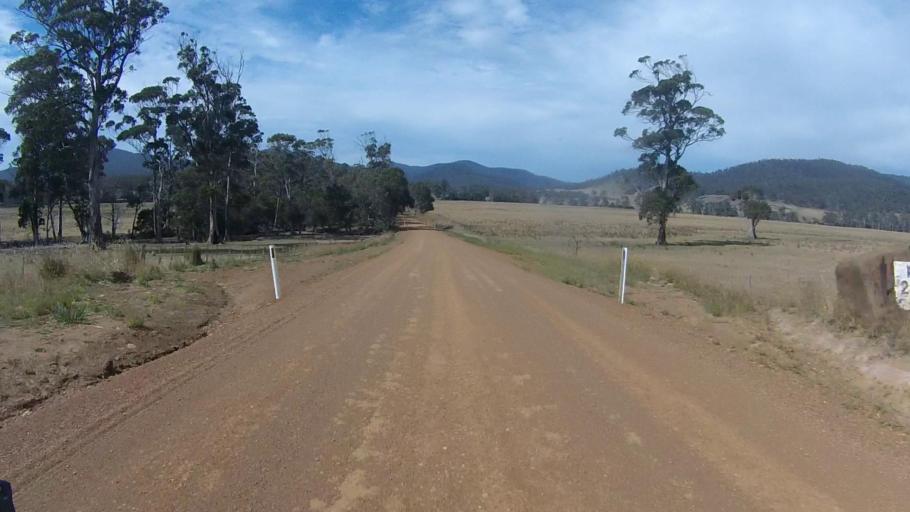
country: AU
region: Tasmania
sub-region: Sorell
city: Sorell
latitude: -42.6342
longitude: 147.9007
